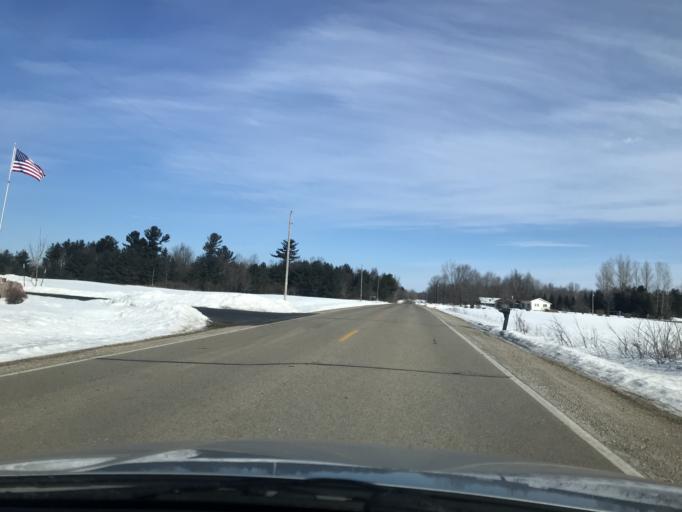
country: US
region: Wisconsin
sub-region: Oconto County
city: Oconto Falls
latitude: 44.9209
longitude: -88.1548
